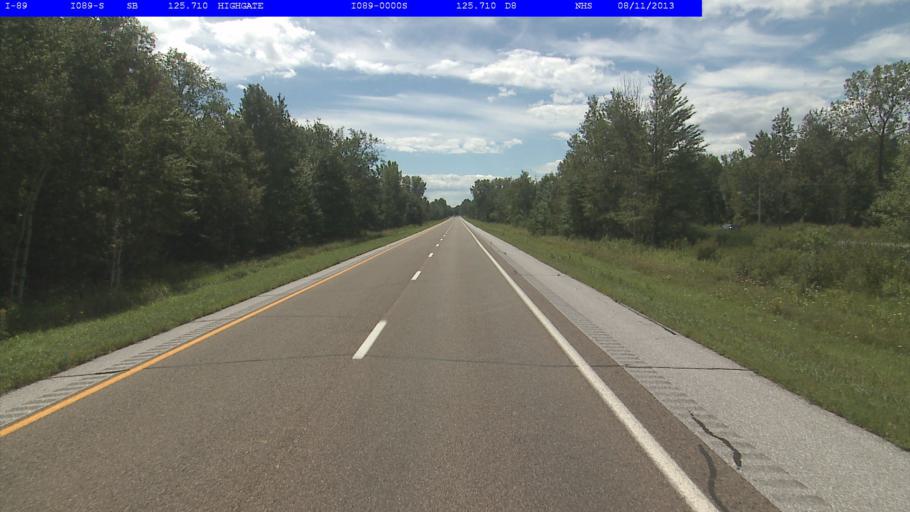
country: US
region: Vermont
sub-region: Franklin County
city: Swanton
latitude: 44.9550
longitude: -73.1109
